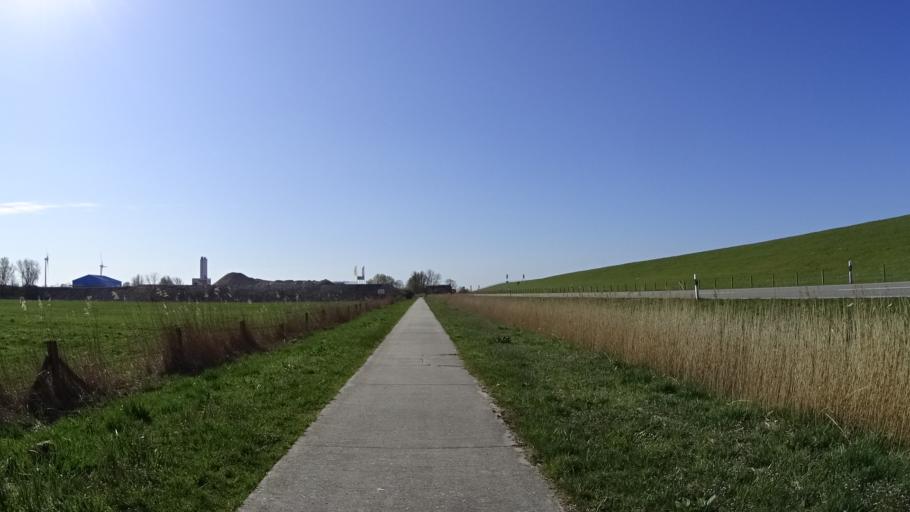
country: DE
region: Lower Saxony
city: Jemgum
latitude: 53.2674
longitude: 7.4076
